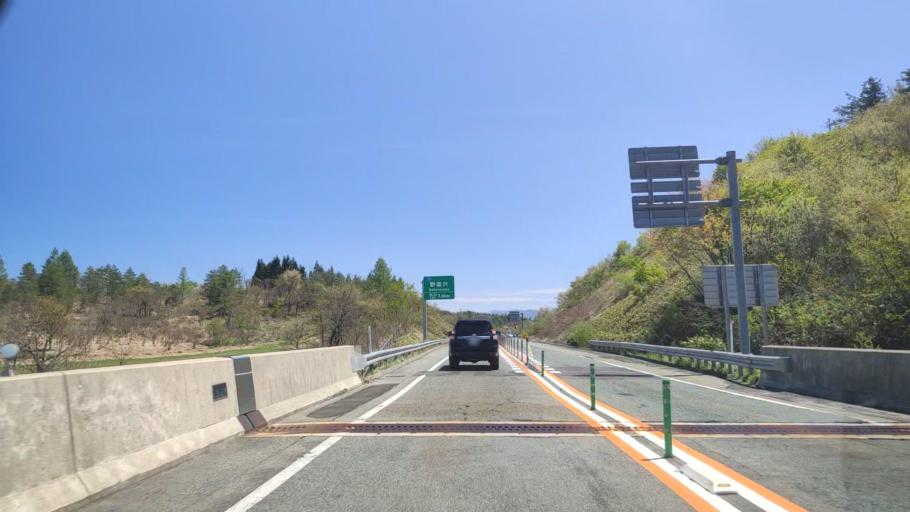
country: JP
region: Yamagata
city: Obanazawa
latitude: 38.6532
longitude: 140.3688
